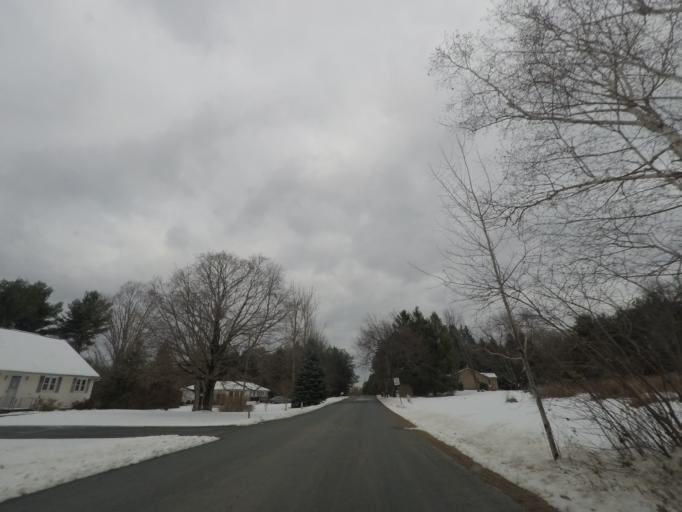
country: US
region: New York
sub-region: Rensselaer County
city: West Sand Lake
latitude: 42.6043
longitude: -73.6303
